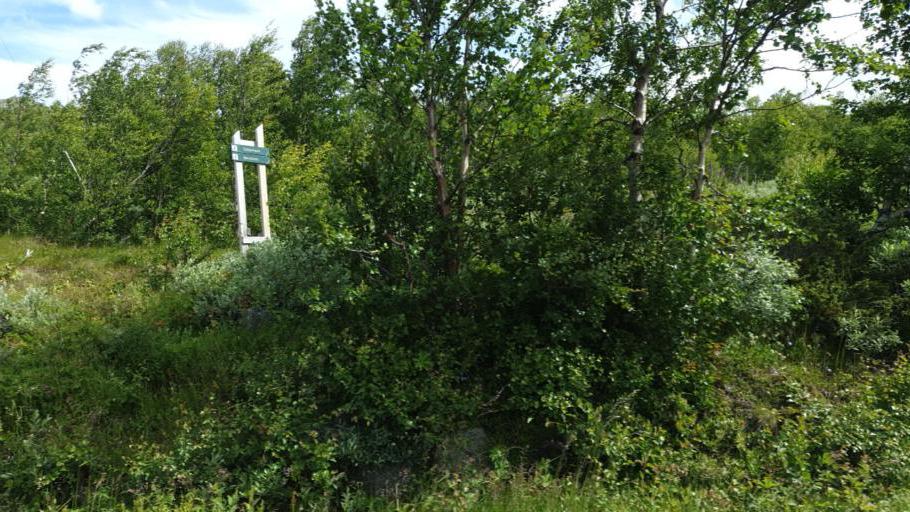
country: NO
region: Oppland
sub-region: Lom
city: Fossbergom
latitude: 61.4933
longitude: 8.8151
